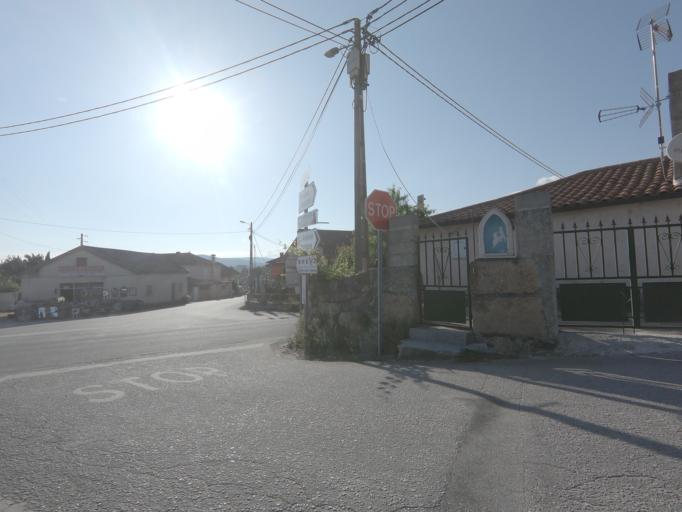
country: PT
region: Vila Real
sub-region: Chaves
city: Chaves
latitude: 41.7915
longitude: -7.4230
